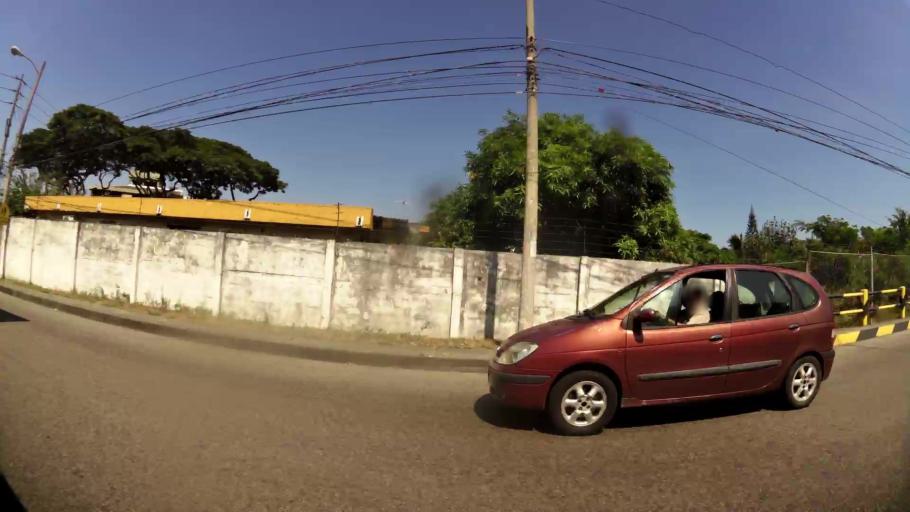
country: EC
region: Guayas
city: Guayaquil
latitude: -2.1632
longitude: -79.9171
